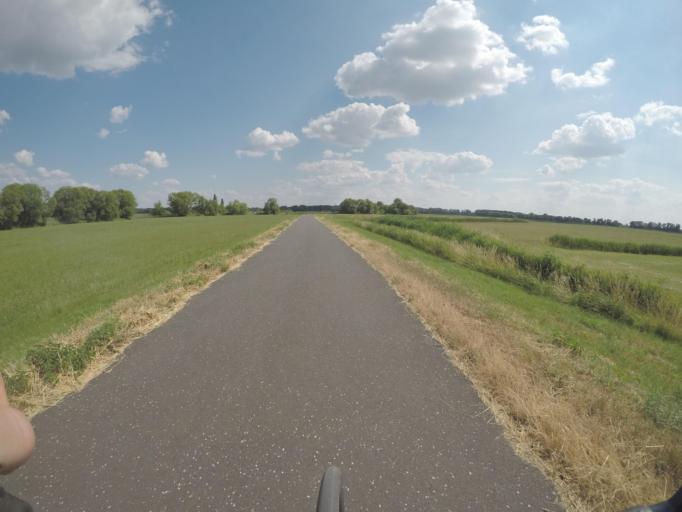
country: DE
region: Brandenburg
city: Ketzin
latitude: 52.4513
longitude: 12.8741
